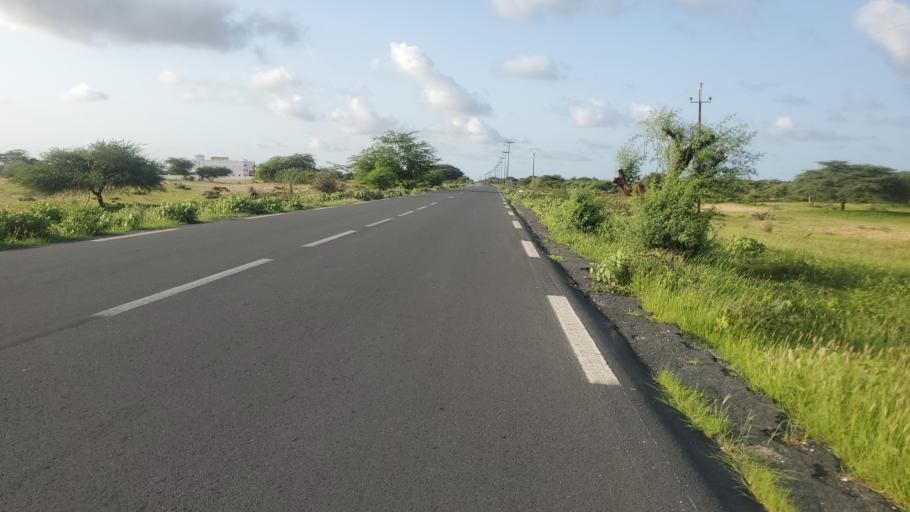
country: SN
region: Saint-Louis
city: Saint-Louis
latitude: 16.1433
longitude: -16.4096
